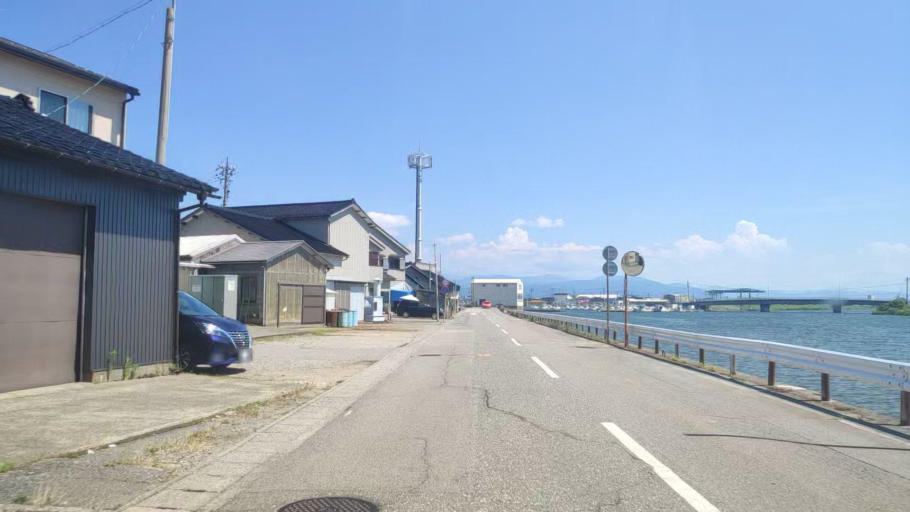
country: JP
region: Ishikawa
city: Kanazawa-shi
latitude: 36.6002
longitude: 136.5890
